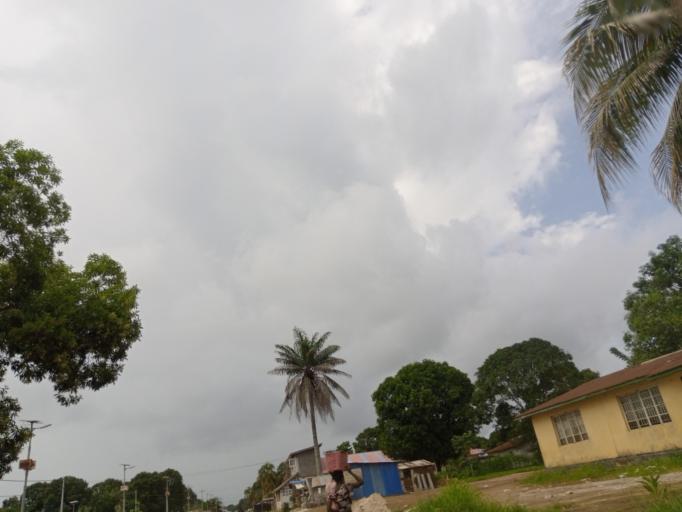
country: SL
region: Northern Province
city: Tintafor
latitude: 8.6255
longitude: -13.2073
